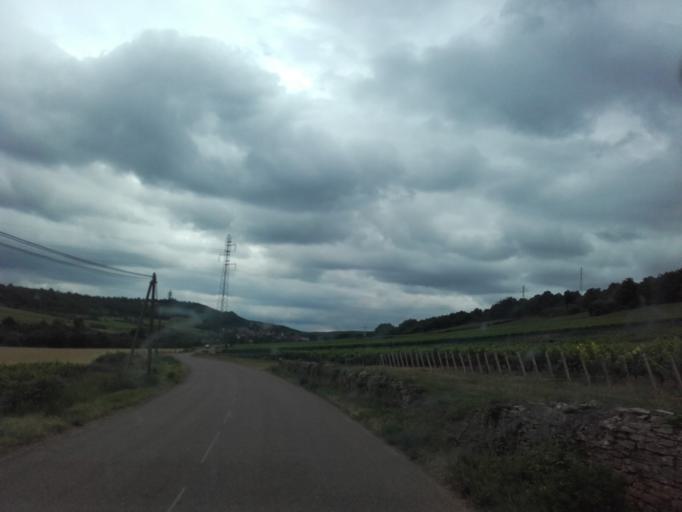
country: FR
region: Bourgogne
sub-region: Departement de Saone-et-Loire
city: Chagny
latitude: 46.9018
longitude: 4.7372
